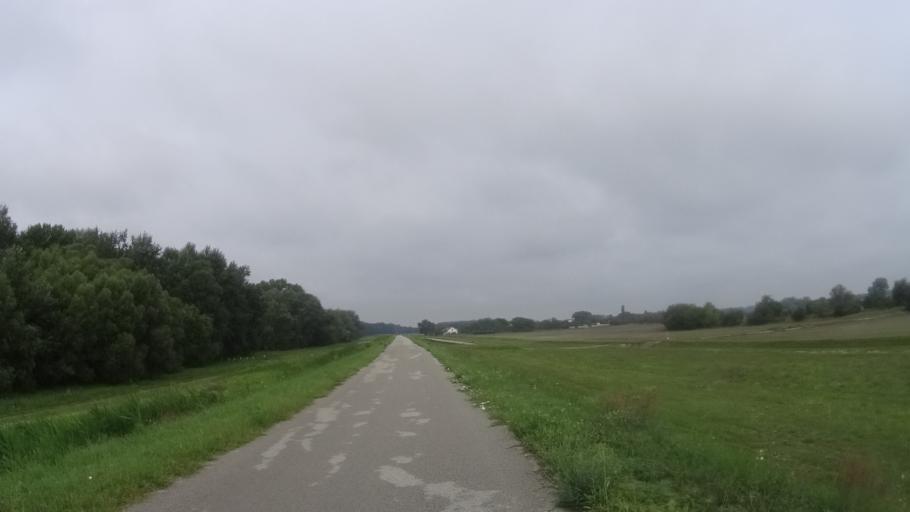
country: SK
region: Nitriansky
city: Komarno
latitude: 47.7467
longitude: 18.1664
